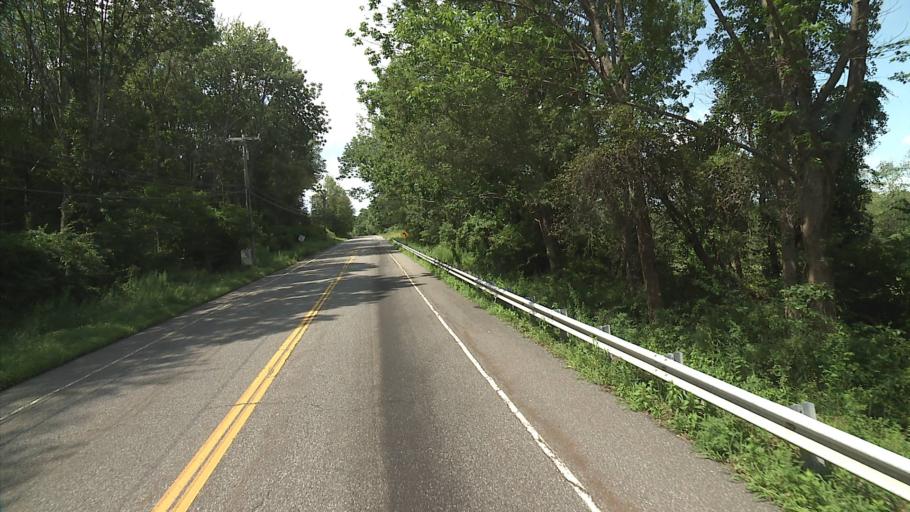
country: US
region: Connecticut
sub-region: New London County
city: Colchester
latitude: 41.5134
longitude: -72.2507
